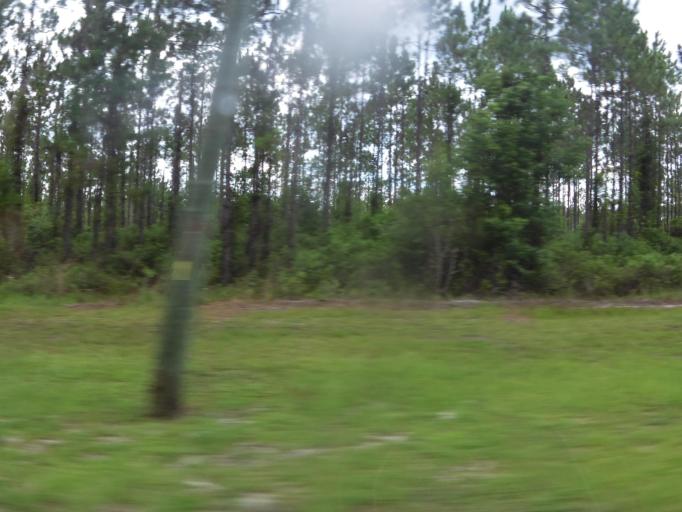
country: US
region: Georgia
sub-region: Camden County
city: Kingsland
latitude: 30.7691
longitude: -81.6490
